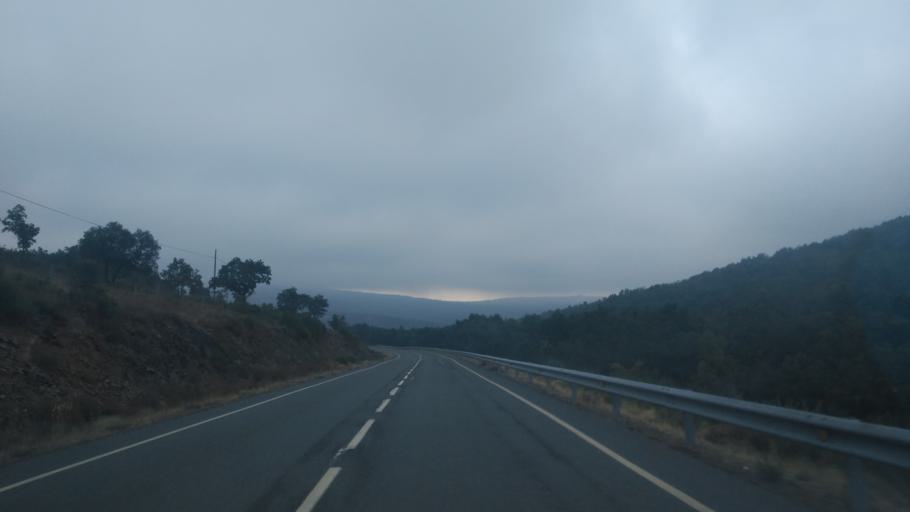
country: ES
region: Castille and Leon
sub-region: Provincia de Salamanca
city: Cereceda de la Sierra
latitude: 40.5873
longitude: -6.0877
